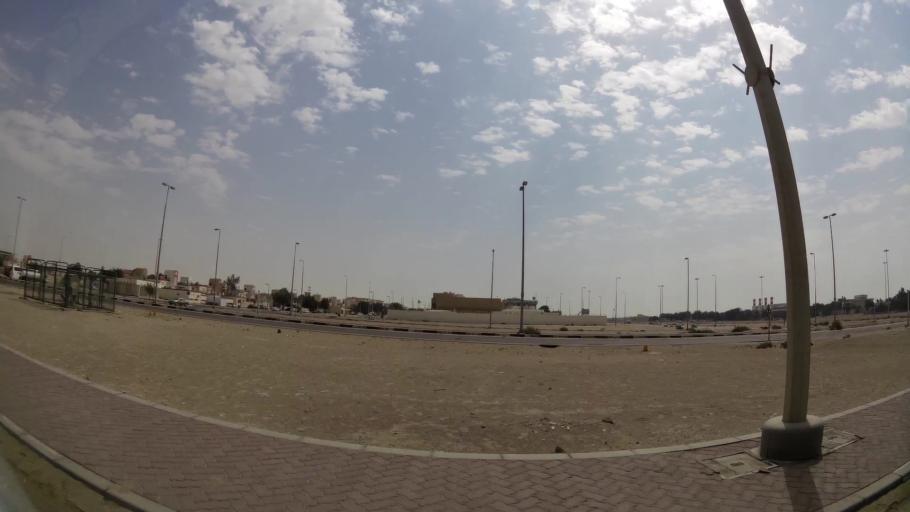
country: AE
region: Abu Dhabi
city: Abu Dhabi
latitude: 24.3083
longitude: 54.6092
